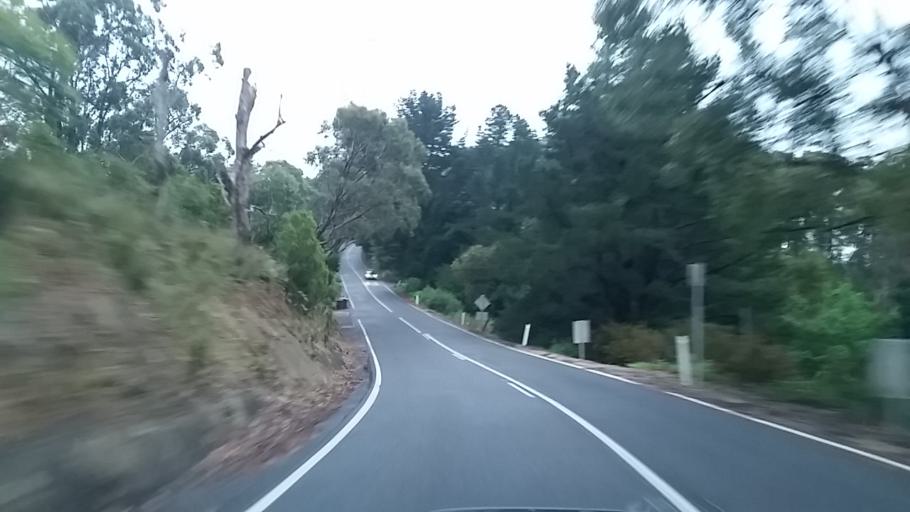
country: AU
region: South Australia
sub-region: Adelaide Hills
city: Crafers
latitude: -34.9856
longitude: 138.7084
